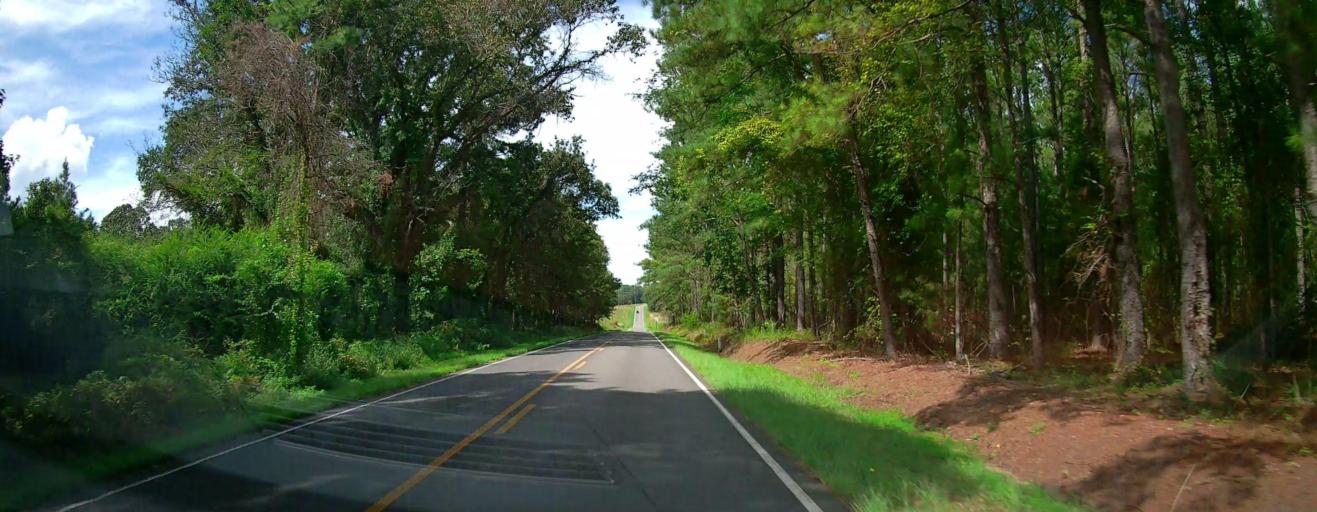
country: US
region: Georgia
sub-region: Taylor County
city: Butler
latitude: 32.5073
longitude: -84.2032
